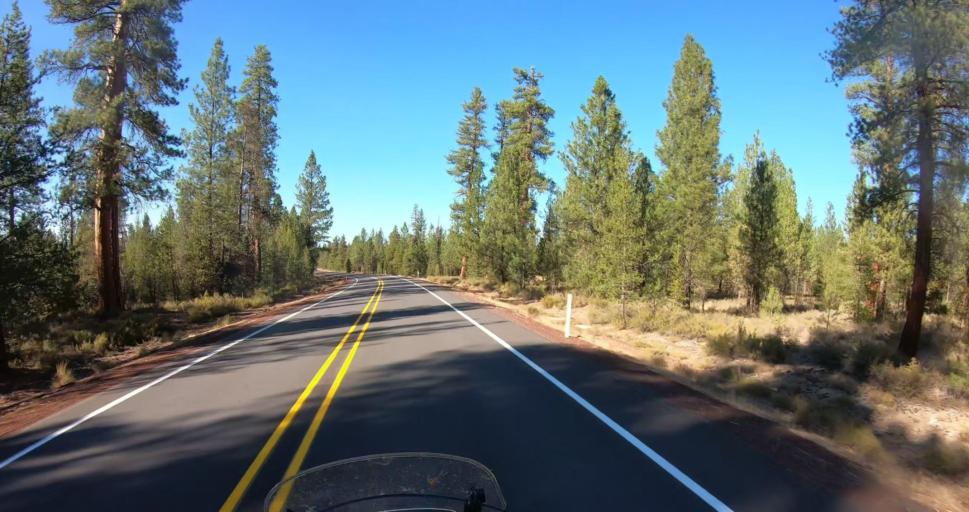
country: US
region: Oregon
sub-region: Deschutes County
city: La Pine
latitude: 43.5110
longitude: -121.4512
